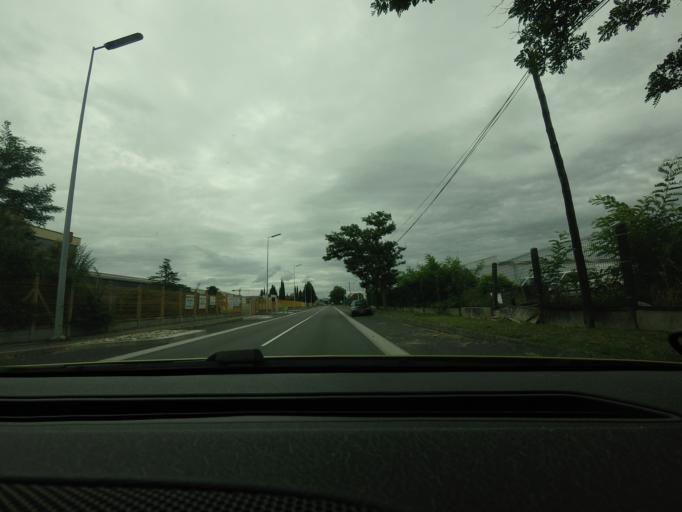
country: FR
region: Midi-Pyrenees
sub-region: Departement de la Haute-Garonne
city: Tournefeuille
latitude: 43.6019
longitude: 1.3085
